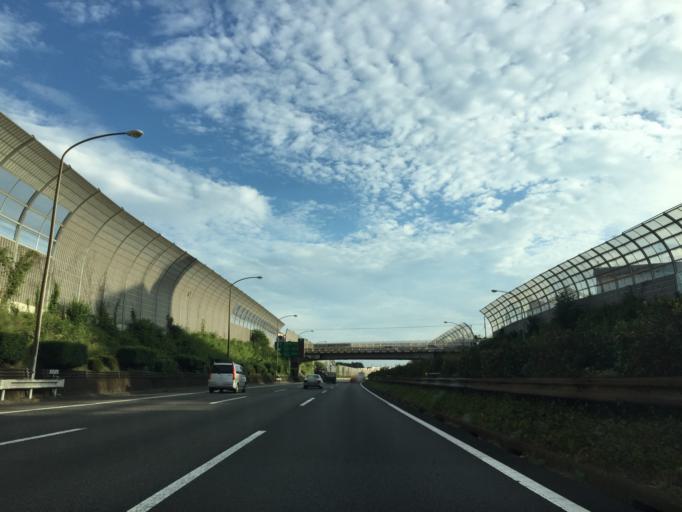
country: JP
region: Kanagawa
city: Minami-rinkan
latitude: 35.4567
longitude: 139.4290
